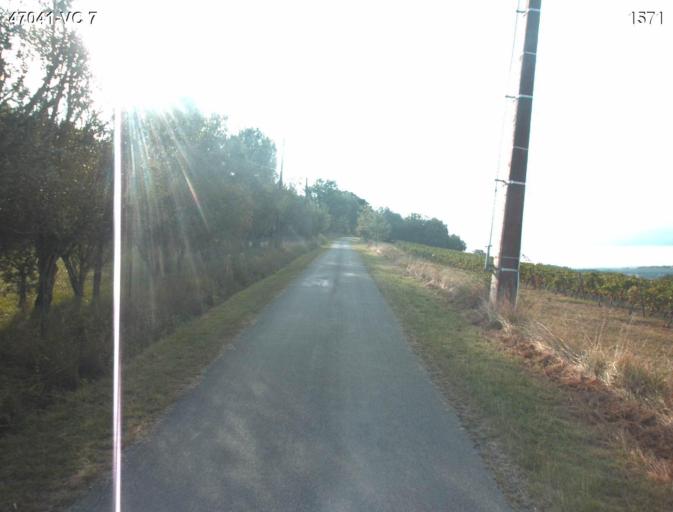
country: FR
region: Aquitaine
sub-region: Departement du Lot-et-Garonne
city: Port-Sainte-Marie
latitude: 44.1962
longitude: 0.4173
